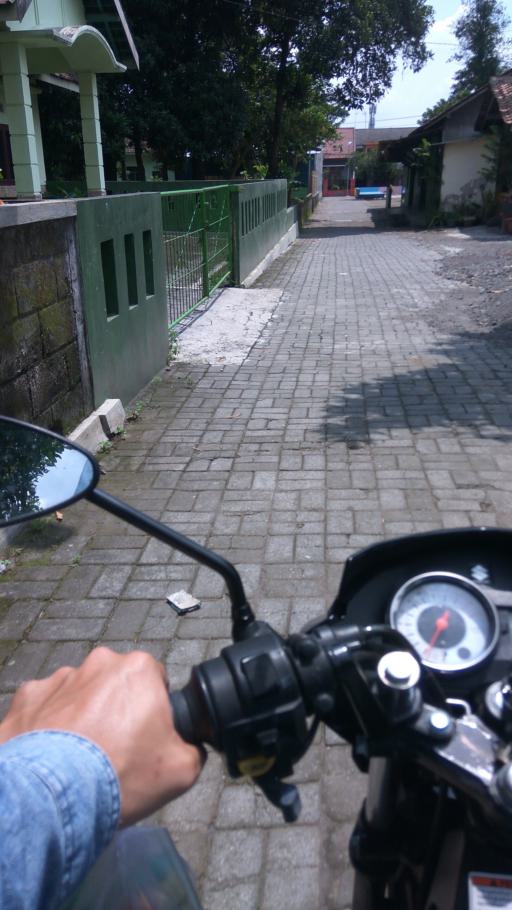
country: ID
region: Daerah Istimewa Yogyakarta
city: Depok
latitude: -7.7498
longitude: 110.4110
